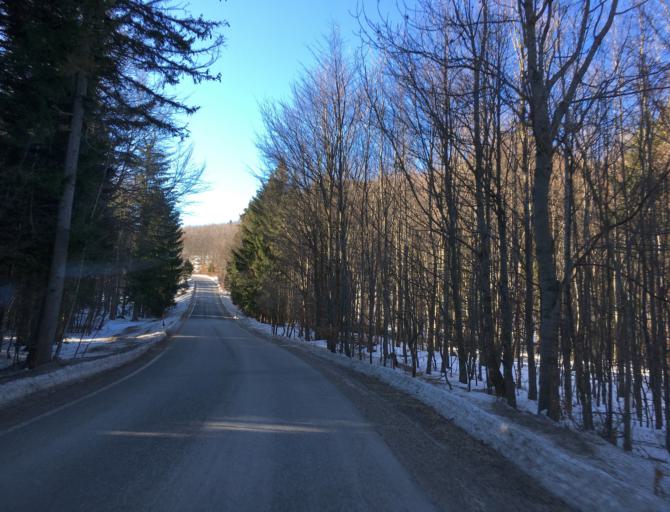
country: AT
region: Lower Austria
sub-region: Politischer Bezirk Wiener Neustadt
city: Waldegg
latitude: 47.8411
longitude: 16.0346
